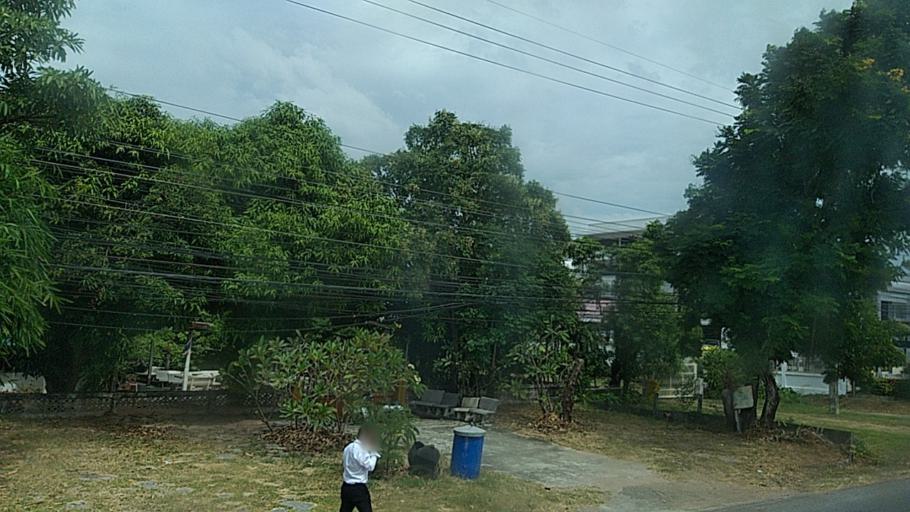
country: TH
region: Roi Et
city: Roi Et
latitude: 16.0676
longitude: 103.6089
